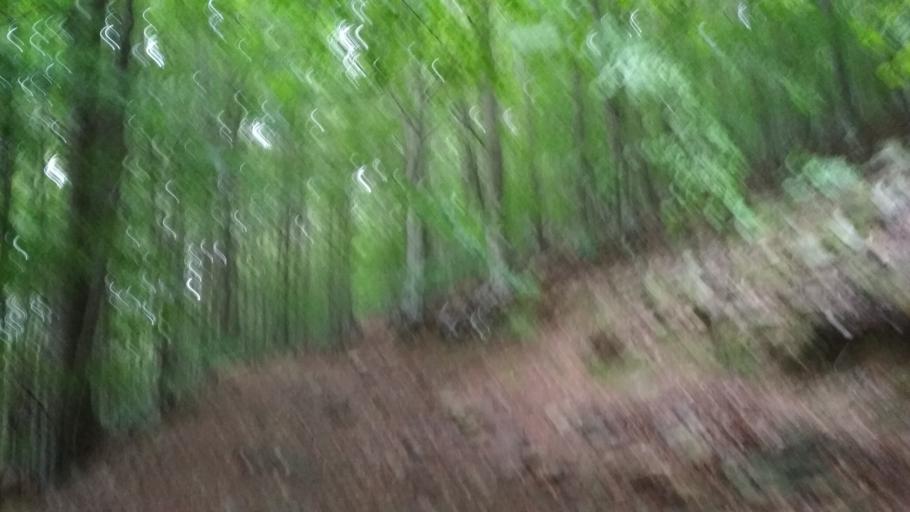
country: ES
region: Catalonia
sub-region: Provincia de Barcelona
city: Fogars de Montclus
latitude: 41.7783
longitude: 2.4494
